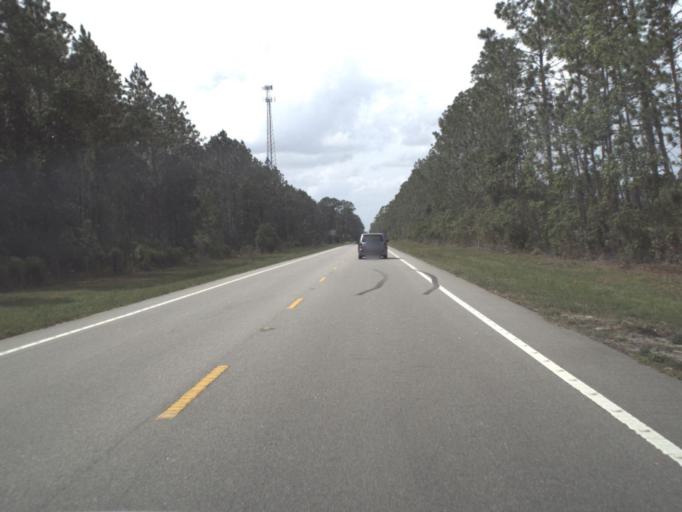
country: US
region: Florida
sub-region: Putnam County
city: Crescent City
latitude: 29.5350
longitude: -81.5186
